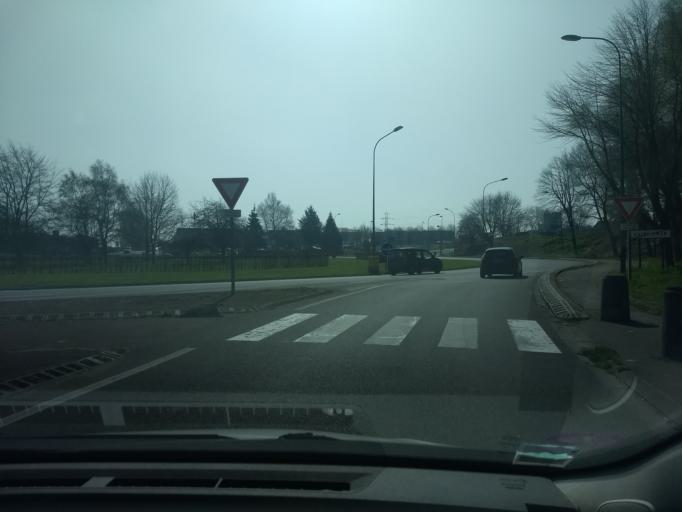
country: FR
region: Nord-Pas-de-Calais
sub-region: Departement du Pas-de-Calais
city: Saint-Omer
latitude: 50.7413
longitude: 2.2577
